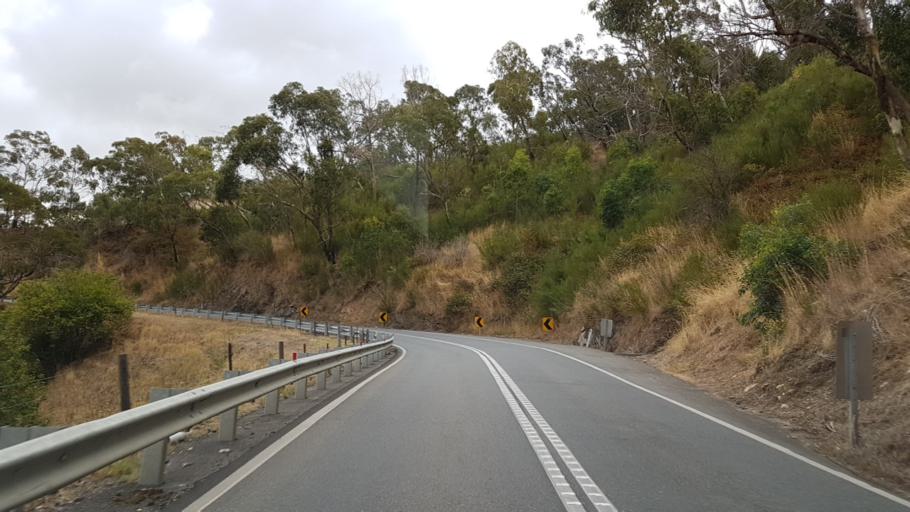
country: AU
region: South Australia
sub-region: Adelaide Hills
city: Gumeracha
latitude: -34.8368
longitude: 138.8240
